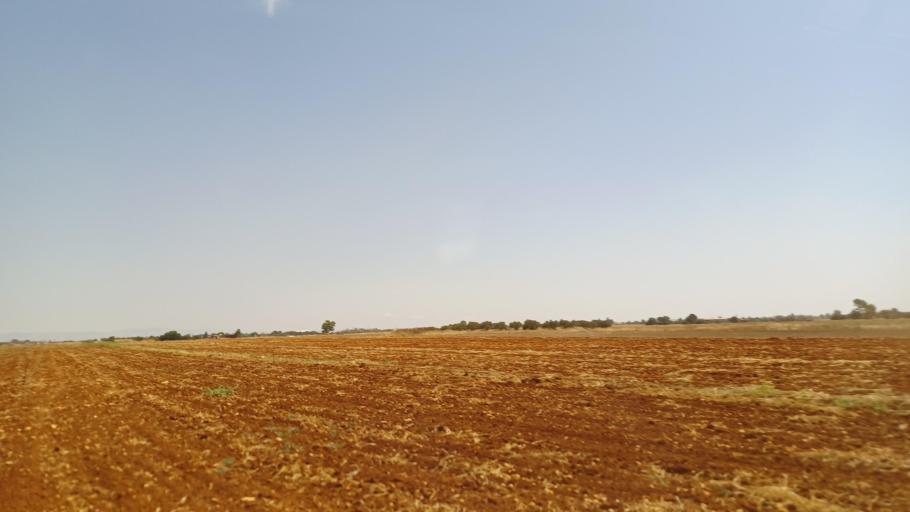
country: CY
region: Ammochostos
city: Avgorou
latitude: 35.0258
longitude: 33.8157
